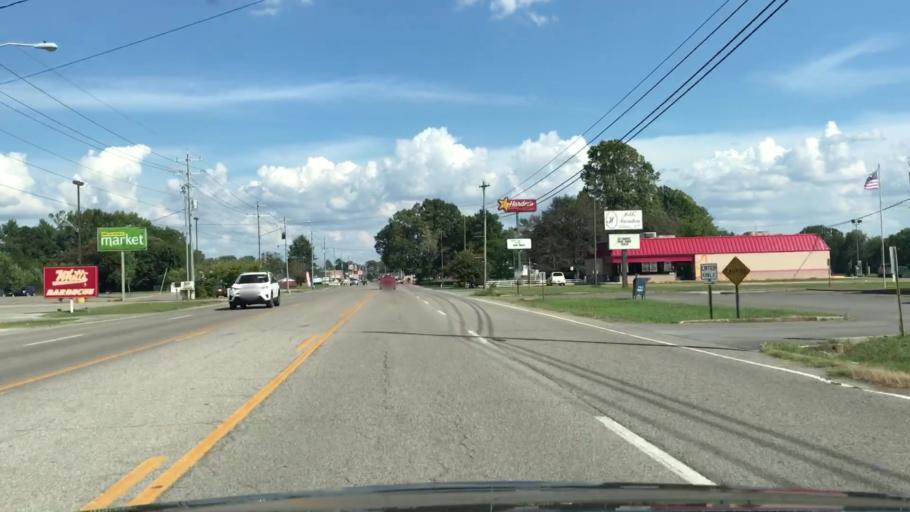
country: US
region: Alabama
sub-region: Limestone County
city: Ardmore
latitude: 34.9946
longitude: -86.8545
